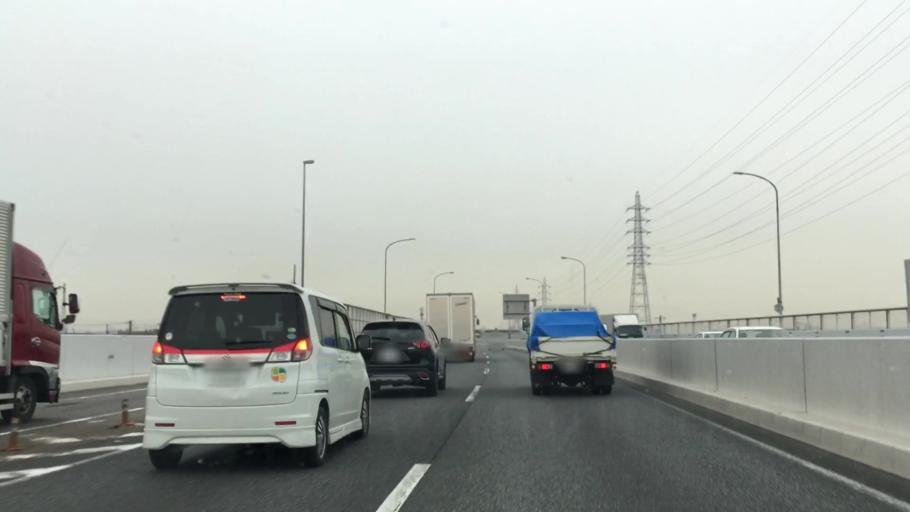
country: JP
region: Aichi
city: Chiryu
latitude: 35.0005
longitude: 137.0287
